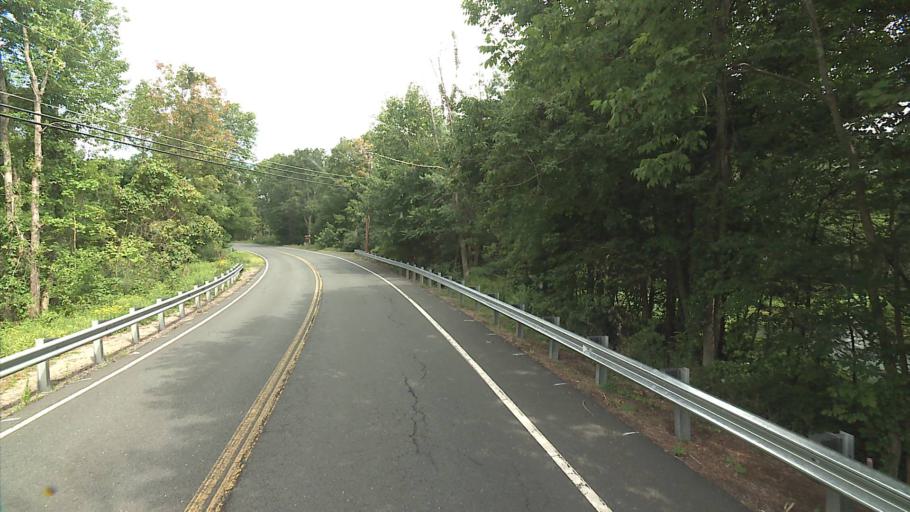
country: US
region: Connecticut
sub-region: Hartford County
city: North Granby
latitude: 42.0150
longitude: -72.8476
